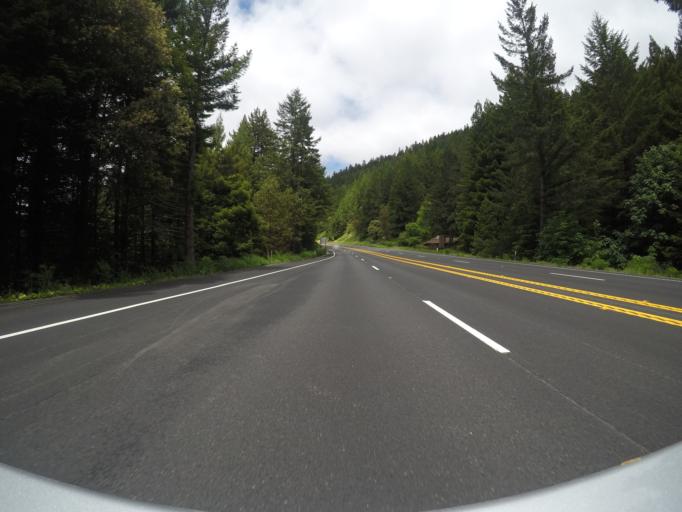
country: US
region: California
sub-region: Humboldt County
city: Redway
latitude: 40.3247
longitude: -123.9216
